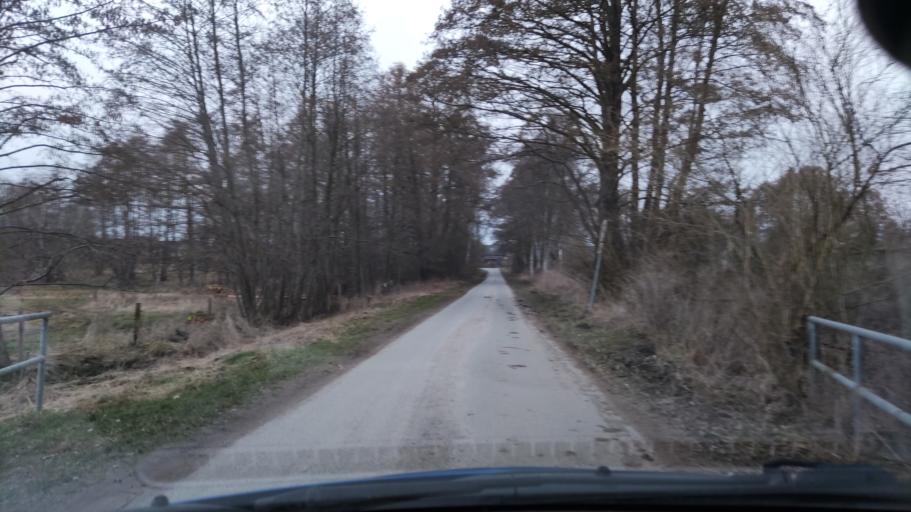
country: DE
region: Lower Saxony
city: Deutsch Evern
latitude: 53.1940
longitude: 10.4368
